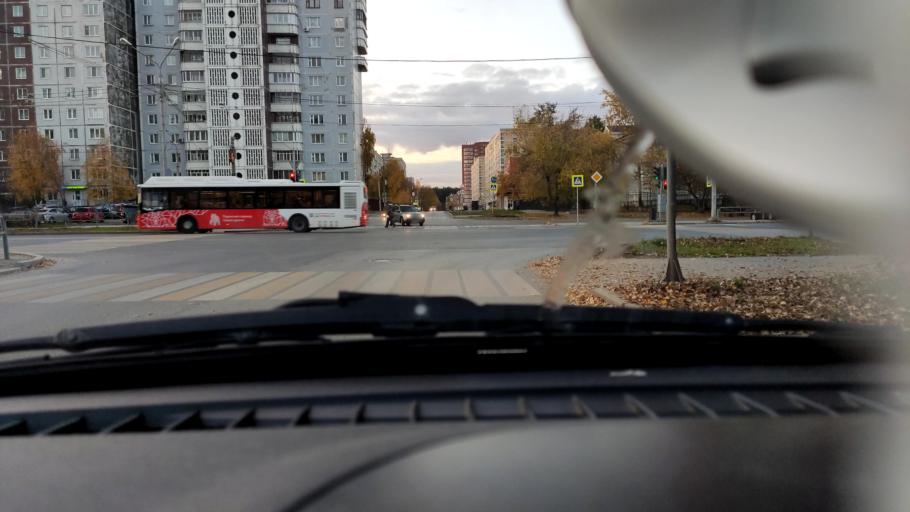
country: RU
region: Perm
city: Kondratovo
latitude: 57.9982
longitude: 56.1471
